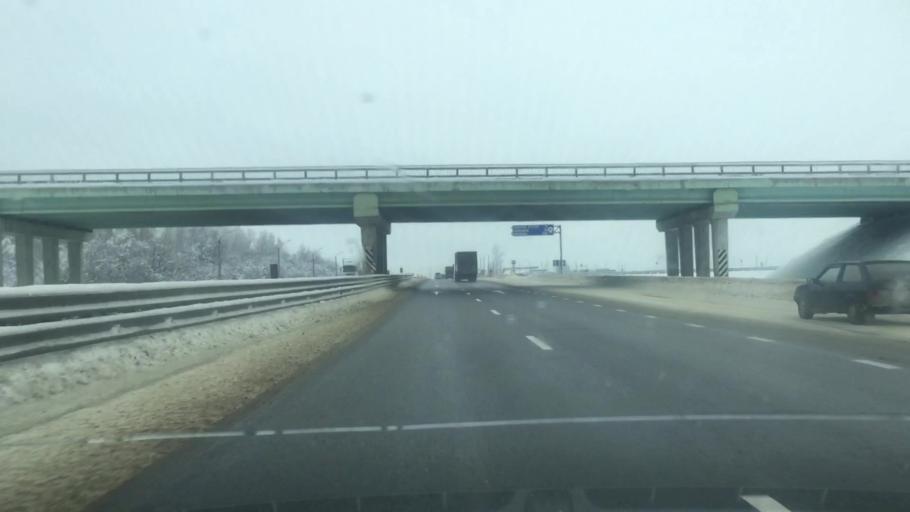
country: RU
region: Tula
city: Kazachka
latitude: 53.3129
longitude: 38.1791
